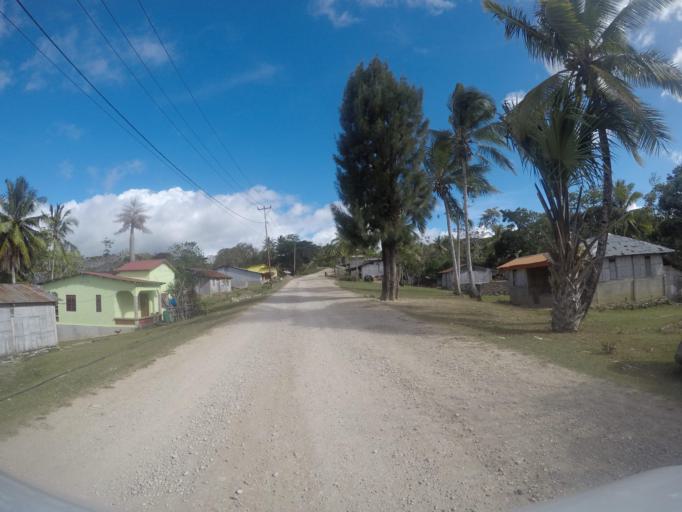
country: TL
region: Lautem
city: Lospalos
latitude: -8.5699
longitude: 126.8840
